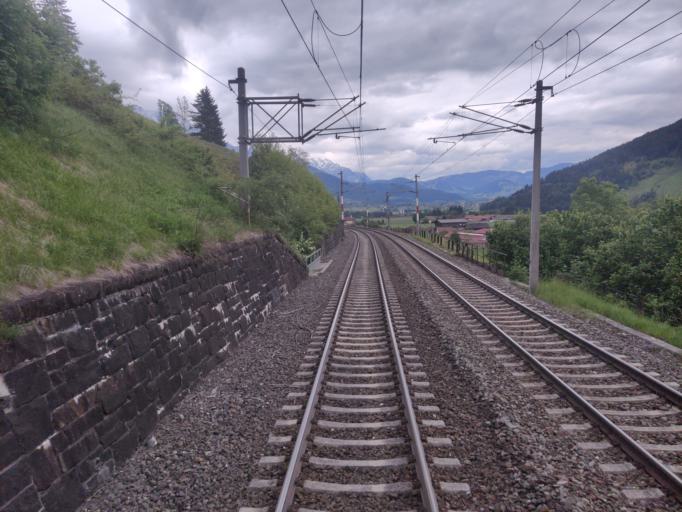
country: AT
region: Salzburg
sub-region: Politischer Bezirk Zell am See
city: Leogang
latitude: 47.4461
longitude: 12.7854
